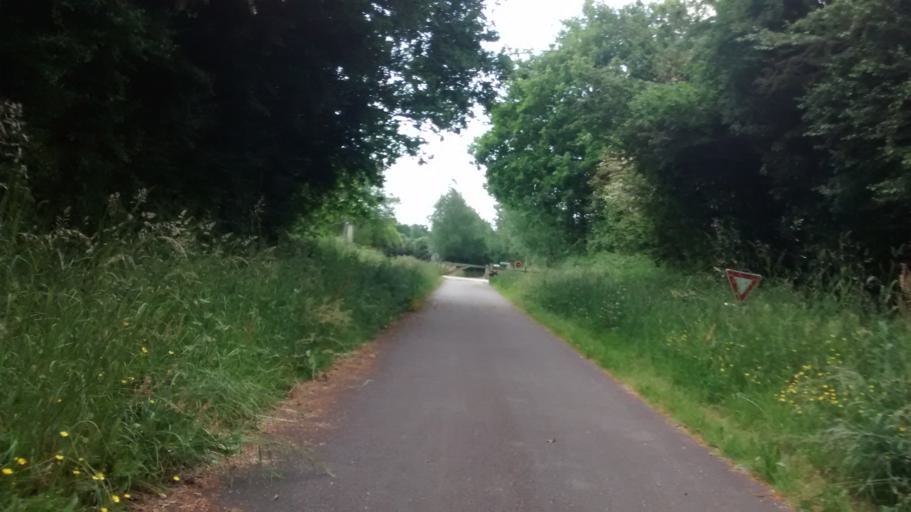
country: FR
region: Brittany
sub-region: Departement du Morbihan
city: Molac
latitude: 47.7104
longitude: -2.4212
